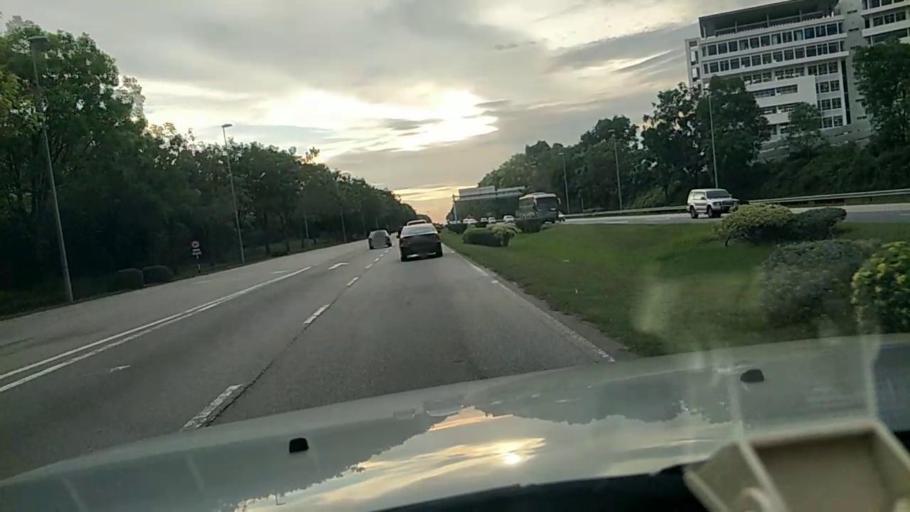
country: MY
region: Selangor
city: Klang
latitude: 3.1079
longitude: 101.4536
